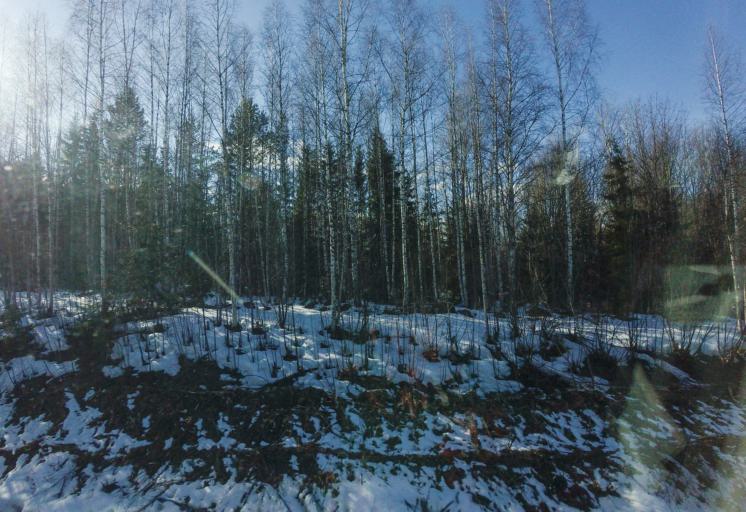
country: FI
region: South Karelia
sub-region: Imatra
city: Parikkala
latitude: 61.4681
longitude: 29.4566
